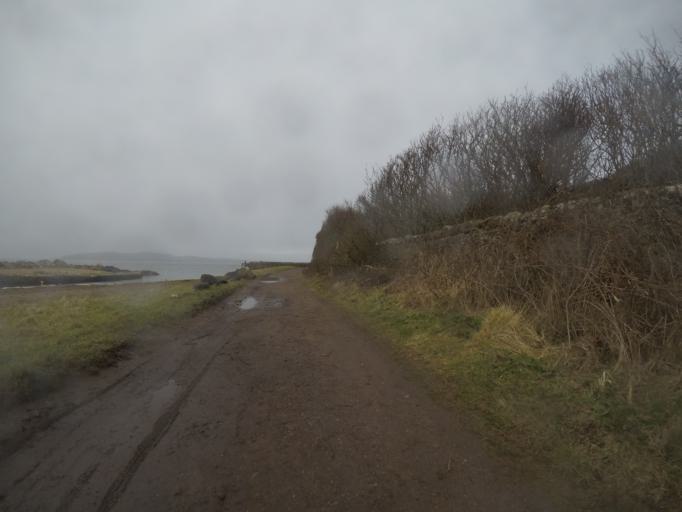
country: GB
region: Scotland
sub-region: North Ayrshire
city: West Kilbride
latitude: 55.7005
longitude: -4.9041
